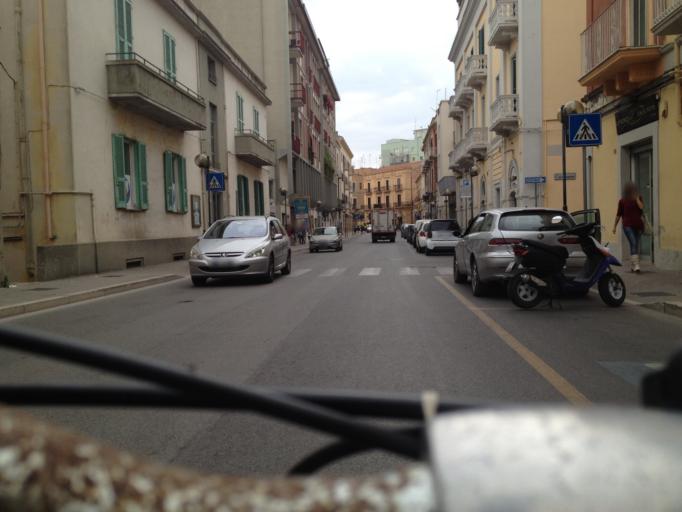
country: IT
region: Basilicate
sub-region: Provincia di Matera
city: Matera
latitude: 40.6683
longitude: 16.6057
